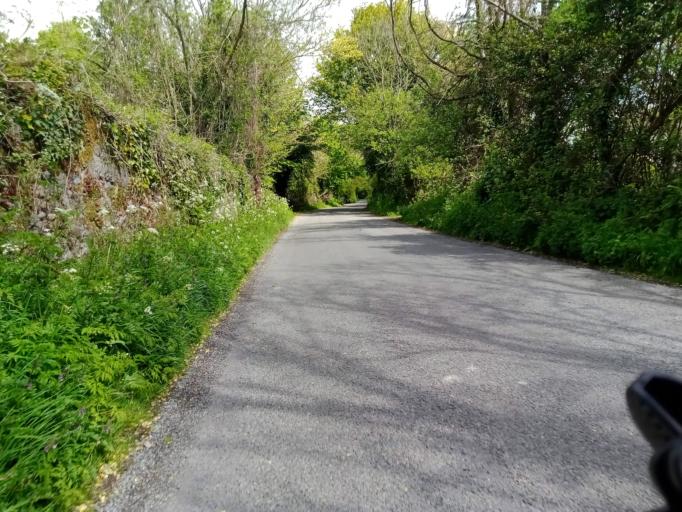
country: IE
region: Leinster
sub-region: Kilkenny
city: Kilkenny
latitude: 52.6709
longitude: -7.2603
